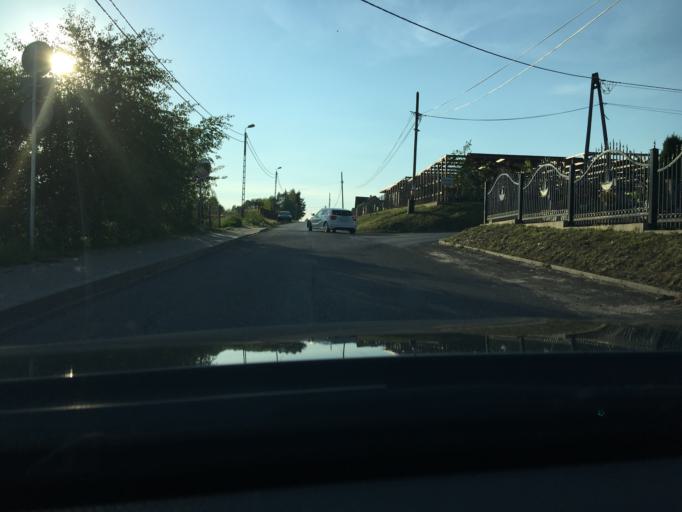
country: PL
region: Lesser Poland Voivodeship
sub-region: Powiat krakowski
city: Jerzmanowice
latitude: 50.2158
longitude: 19.7434
